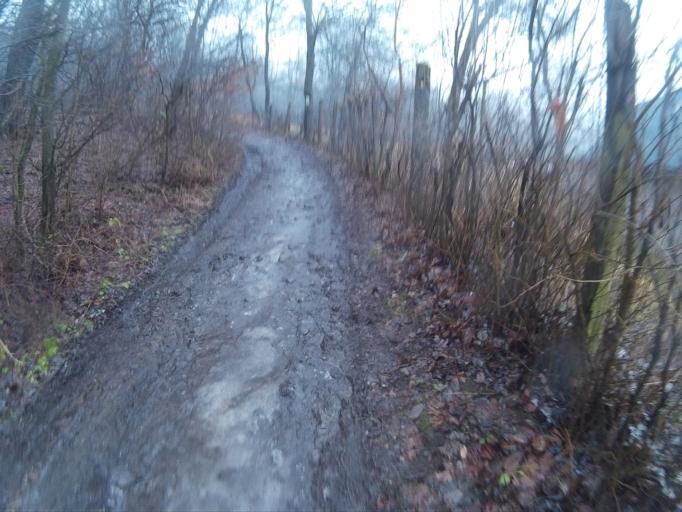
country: HU
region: Nograd
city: Somoskoujfalu
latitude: 48.1664
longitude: 19.8576
